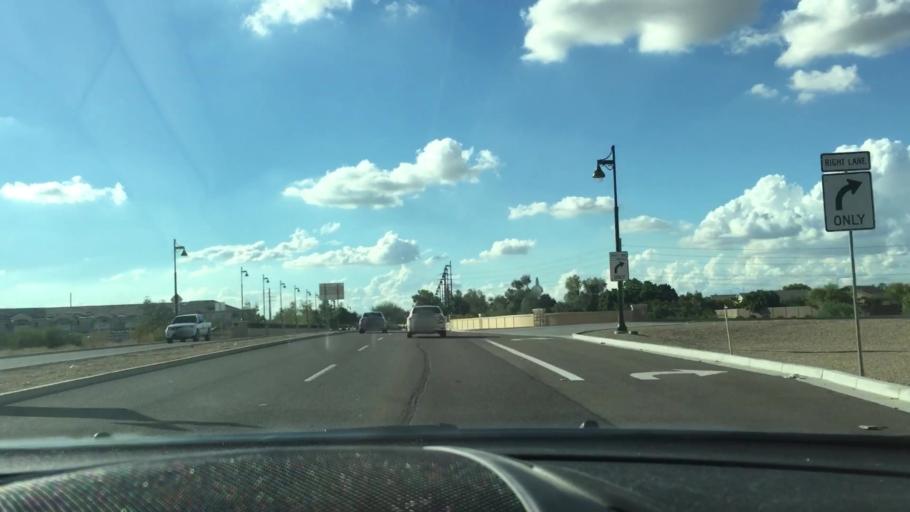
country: US
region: Arizona
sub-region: Maricopa County
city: Sun City
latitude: 33.6659
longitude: -112.2296
